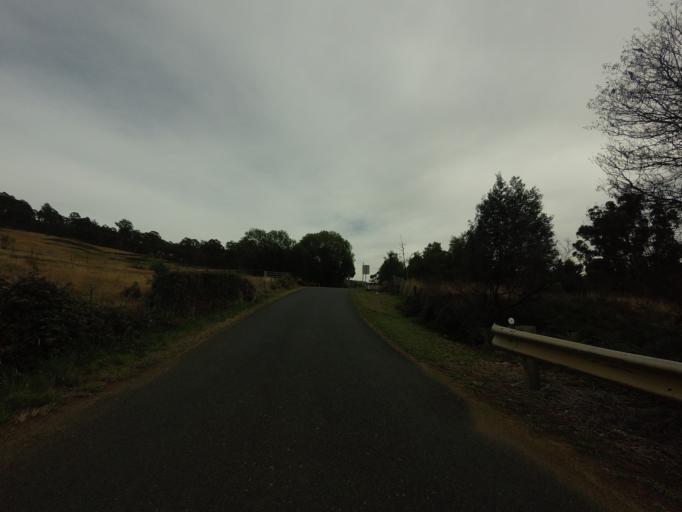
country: AU
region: Tasmania
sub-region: Sorell
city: Sorell
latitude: -42.4919
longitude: 147.5673
